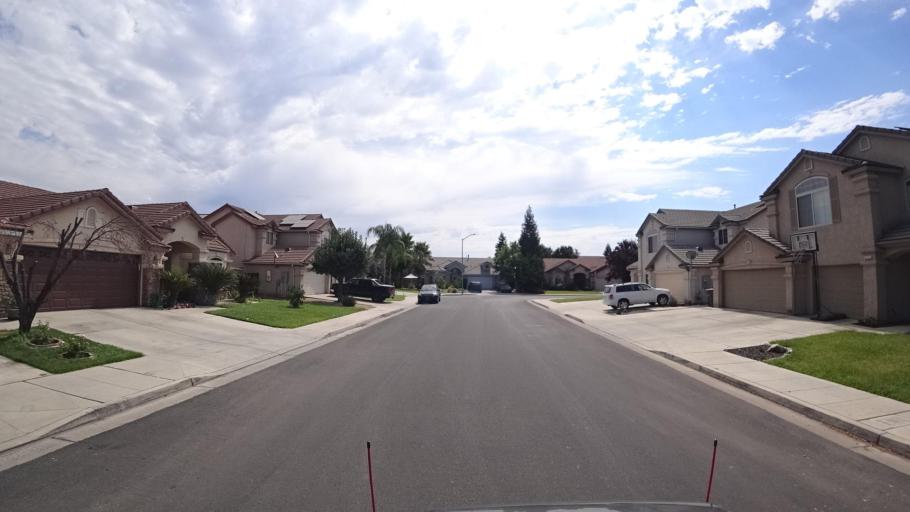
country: US
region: California
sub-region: Fresno County
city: Tarpey Village
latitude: 36.7788
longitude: -119.6695
